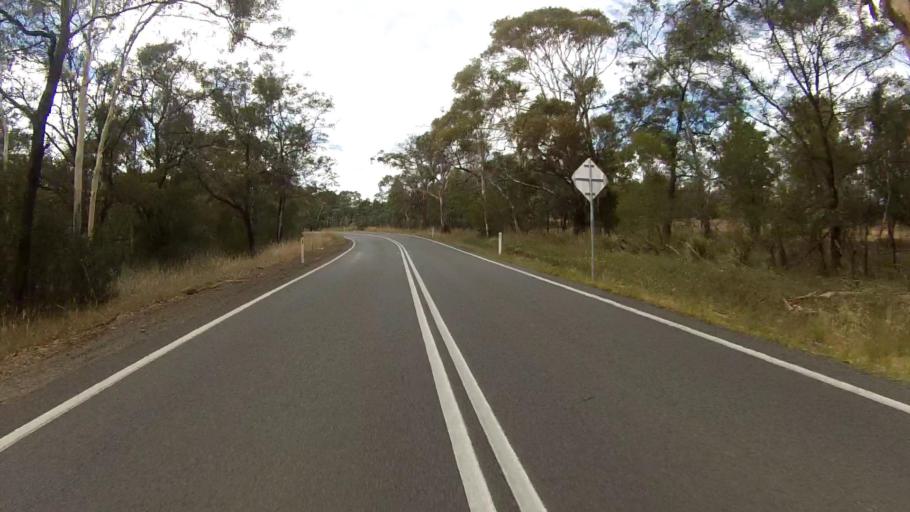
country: AU
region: Tasmania
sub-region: Sorell
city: Sorell
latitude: -42.7017
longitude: 147.4892
